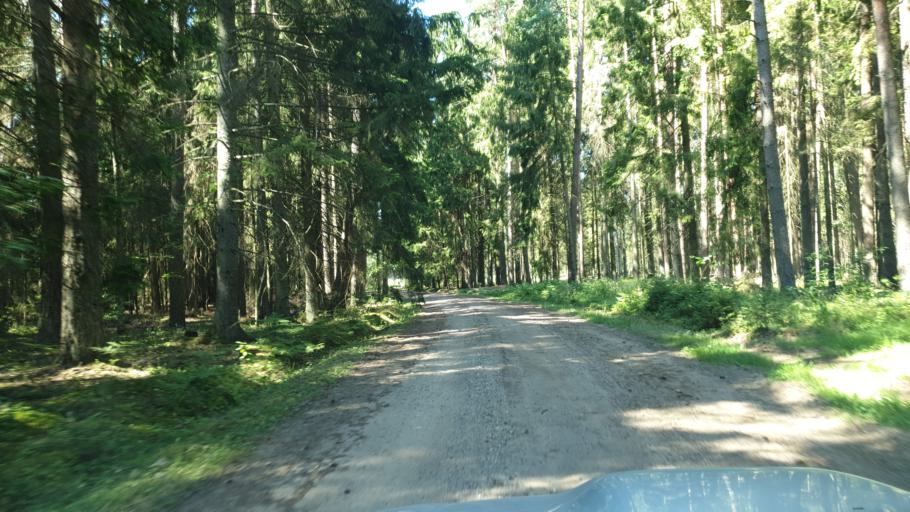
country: LT
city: Sirvintos
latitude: 54.9092
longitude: 24.9382
